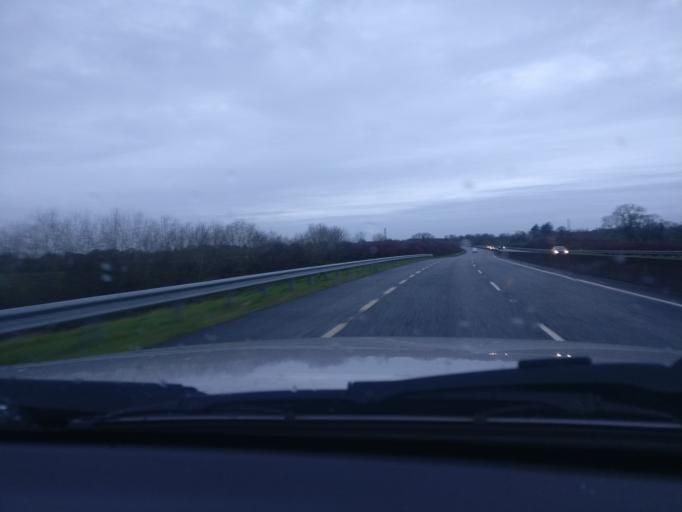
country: IE
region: Leinster
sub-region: An Mhi
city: Navan
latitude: 53.6464
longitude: -6.7216
